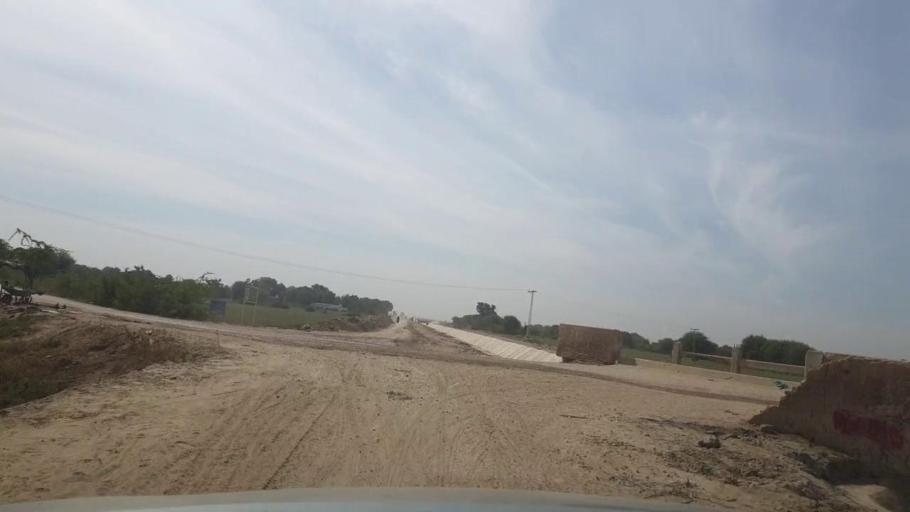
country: PK
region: Sindh
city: Kunri
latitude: 25.1448
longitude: 69.5880
